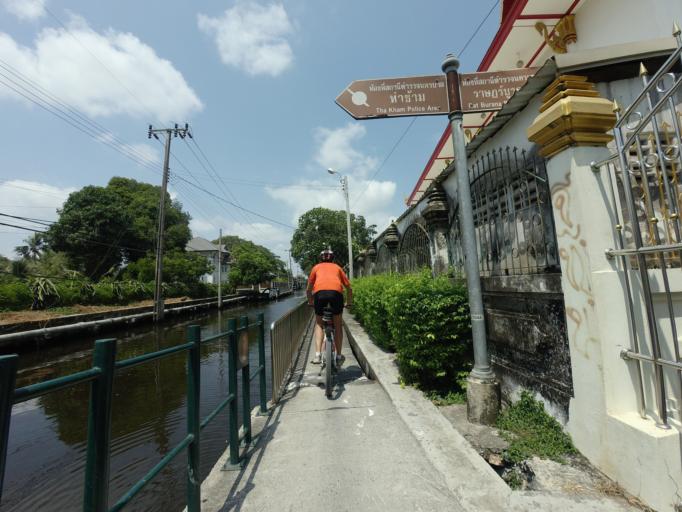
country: TH
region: Bangkok
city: Chom Thong
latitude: 13.6498
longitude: 100.4722
